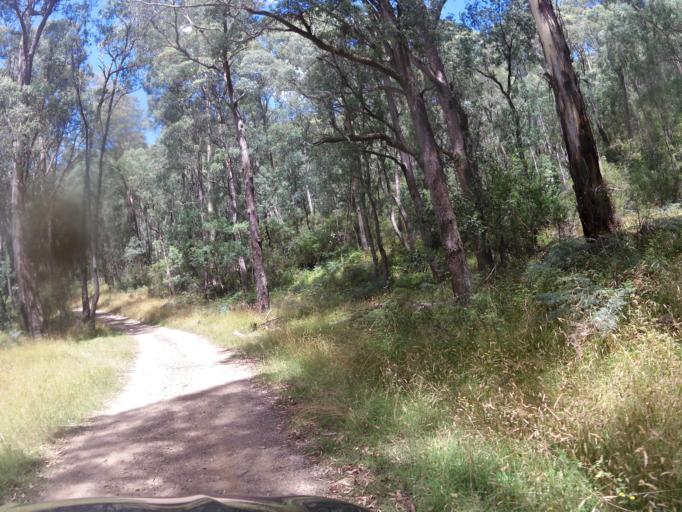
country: AU
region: Victoria
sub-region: Alpine
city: Mount Beauty
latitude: -36.7816
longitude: 147.0690
